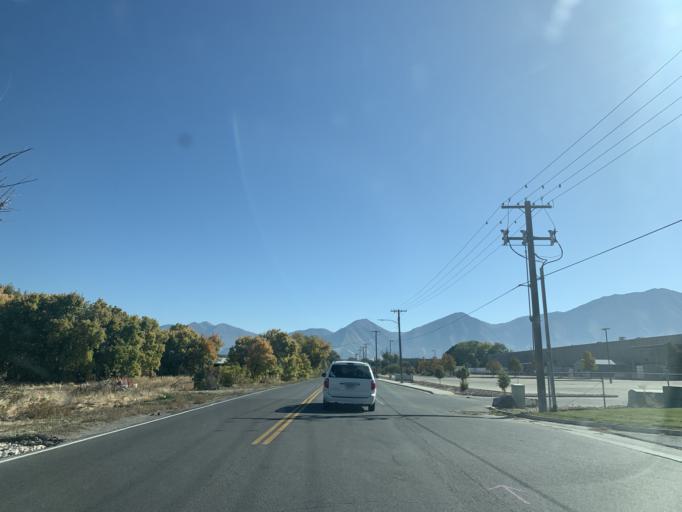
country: US
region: Utah
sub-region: Utah County
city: Payson
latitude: 40.0437
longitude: -111.7543
